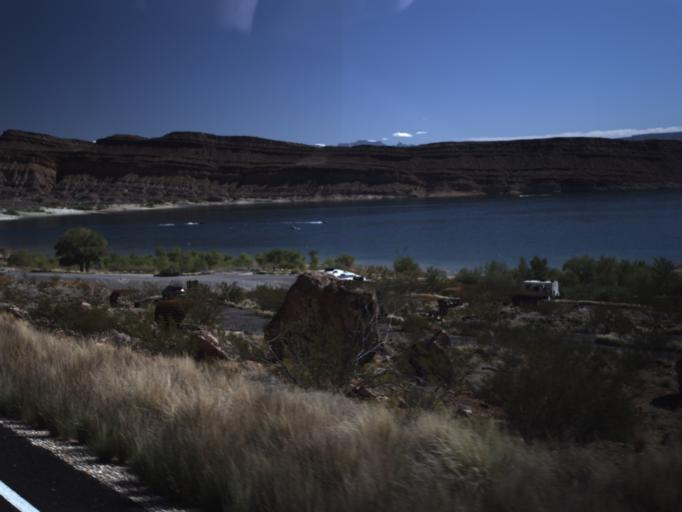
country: US
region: Utah
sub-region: Washington County
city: Hurricane
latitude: 37.1869
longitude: -113.3966
